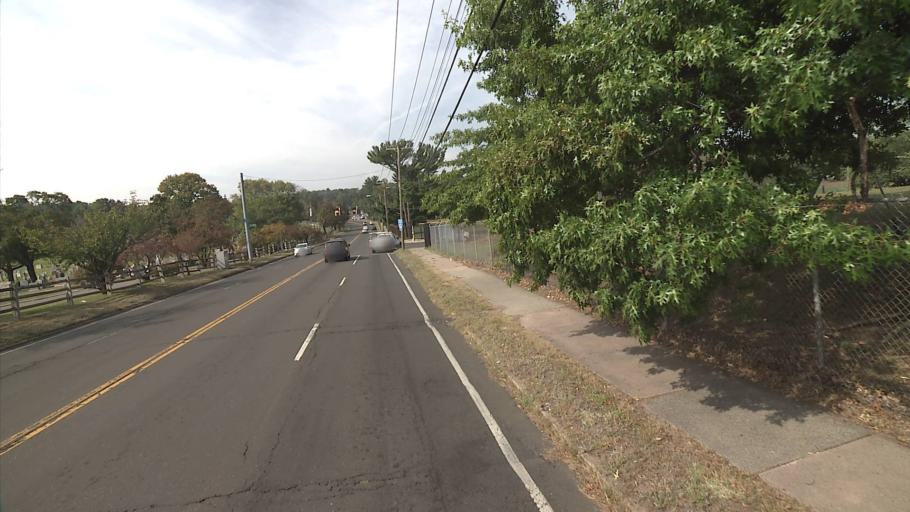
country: US
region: Connecticut
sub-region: New Haven County
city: New Haven
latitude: 41.3096
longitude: -72.9633
